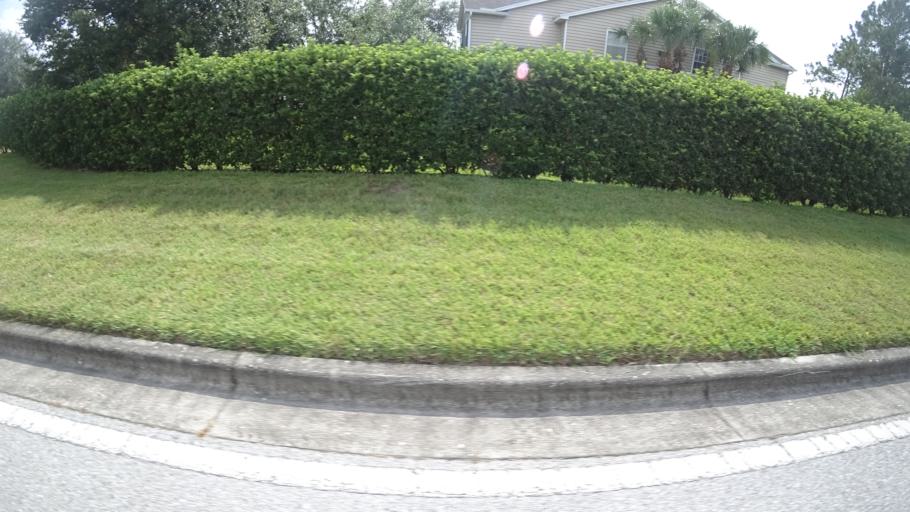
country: US
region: Florida
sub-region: Sarasota County
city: The Meadows
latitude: 27.4033
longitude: -82.4499
